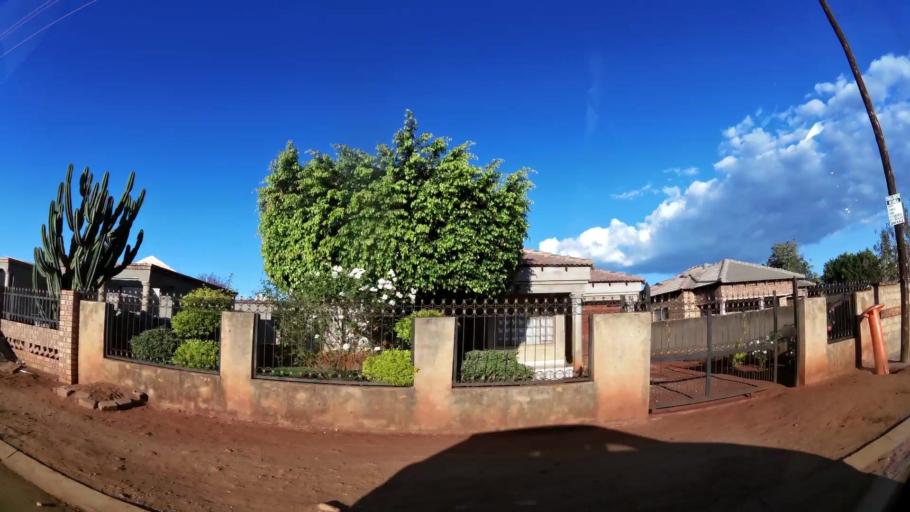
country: ZA
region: Limpopo
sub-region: Waterberg District Municipality
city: Mokopane
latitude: -24.1525
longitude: 28.9939
